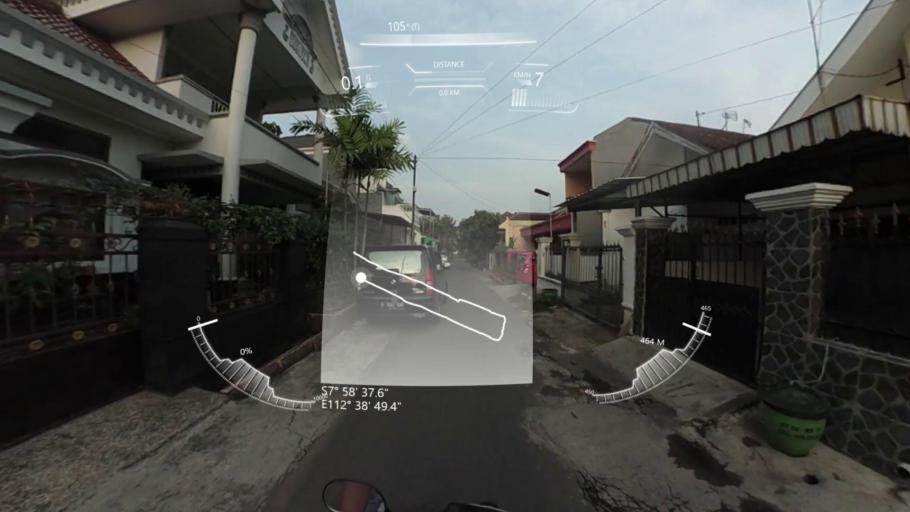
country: ID
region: East Java
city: Malang
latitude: -7.9771
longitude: 112.6470
